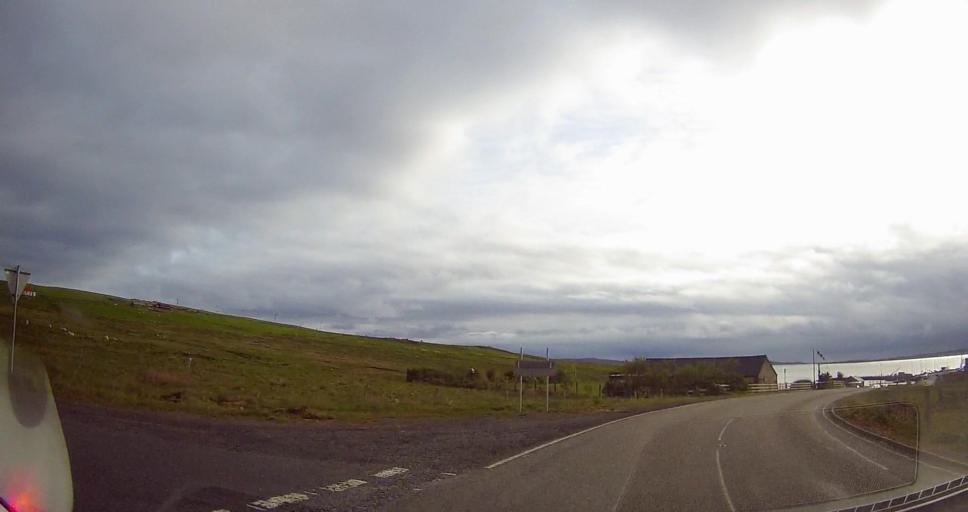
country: GB
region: Scotland
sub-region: Shetland Islands
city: Lerwick
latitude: 60.4663
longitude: -1.2126
